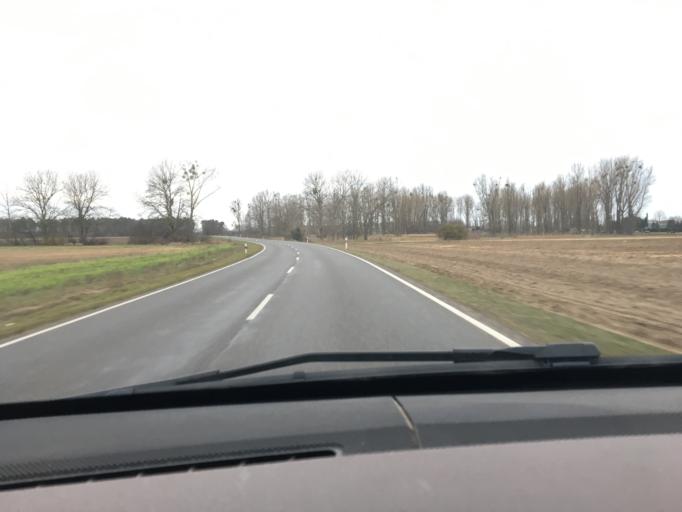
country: DE
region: Brandenburg
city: Liebenwalde
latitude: 52.8792
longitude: 13.4565
